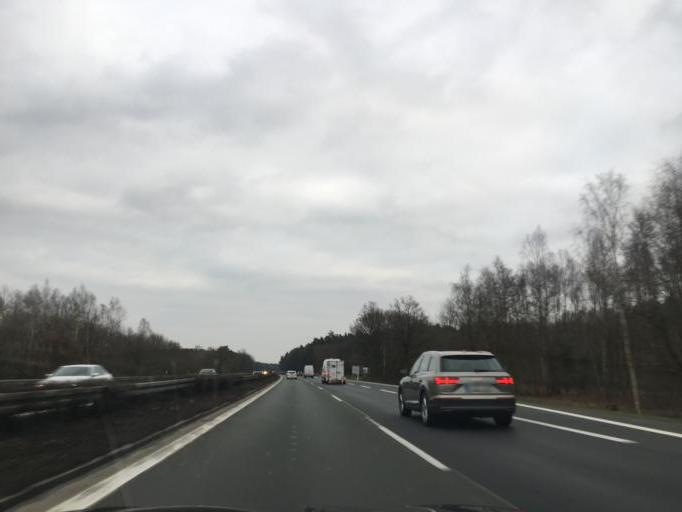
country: DE
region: Bavaria
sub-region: Regierungsbezirk Mittelfranken
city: Grossenseebach
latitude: 49.6707
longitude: 10.8770
